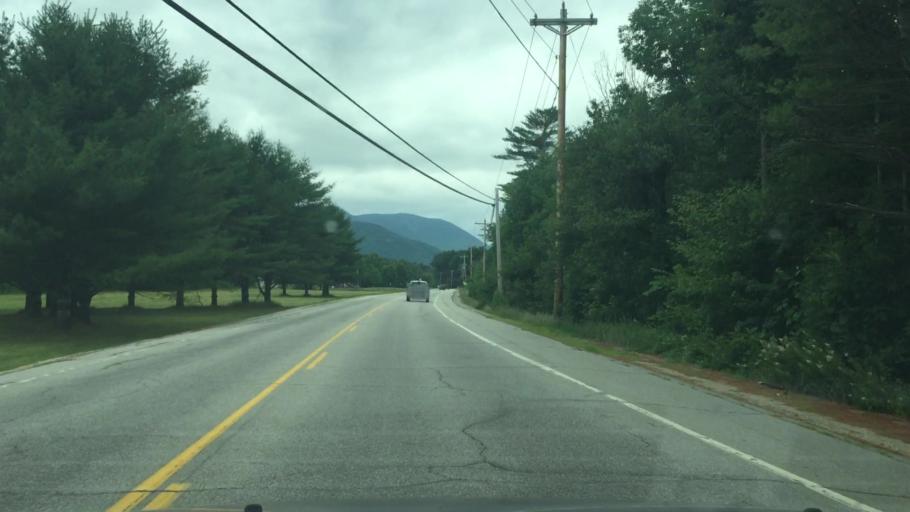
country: US
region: New Hampshire
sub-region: Carroll County
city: North Conway
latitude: 44.0811
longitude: -71.2487
